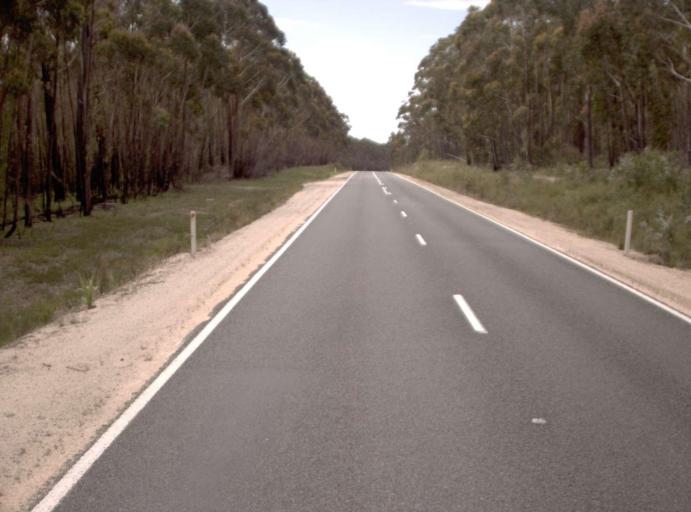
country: AU
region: New South Wales
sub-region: Bega Valley
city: Eden
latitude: -37.5302
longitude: 149.4870
